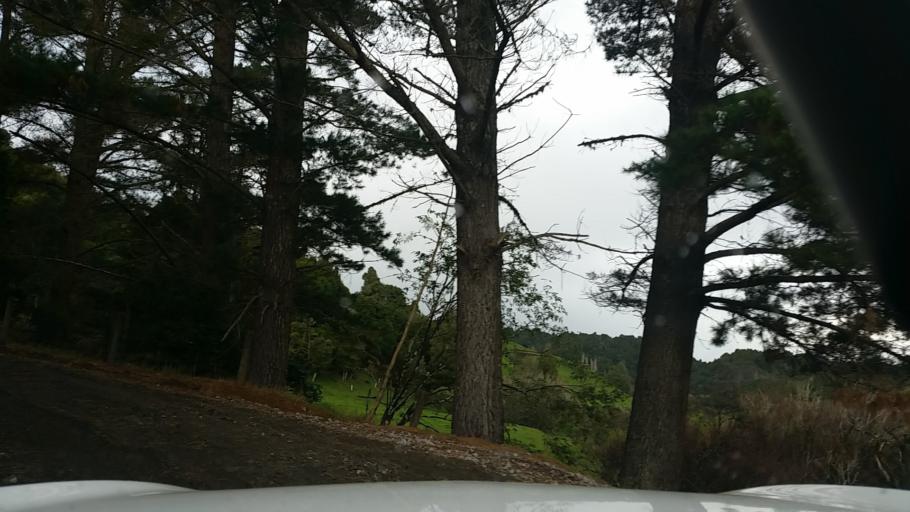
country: NZ
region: Taranaki
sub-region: New Plymouth District
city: Waitara
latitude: -39.1520
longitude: 174.5238
